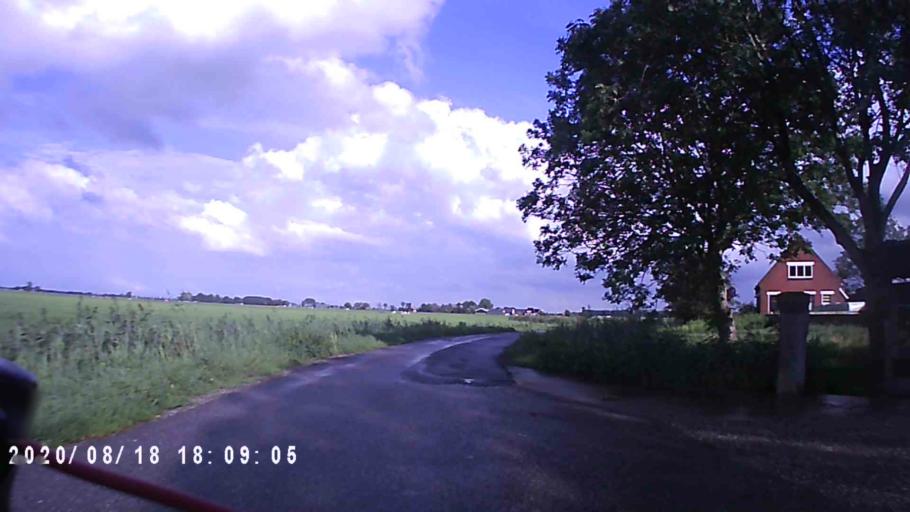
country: NL
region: Groningen
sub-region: Gemeente Zuidhorn
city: Noordhorn
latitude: 53.2816
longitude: 6.4007
